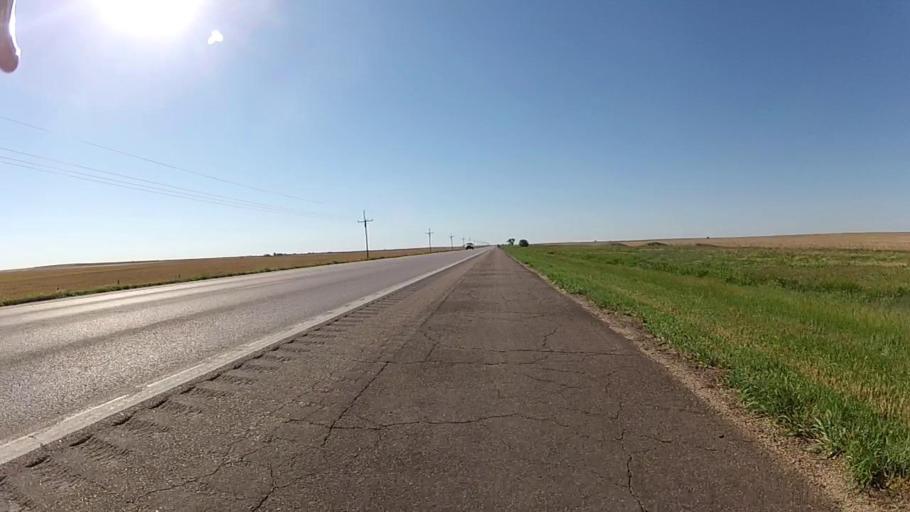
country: US
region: Kansas
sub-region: Ford County
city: Dodge City
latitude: 37.5988
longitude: -99.6990
